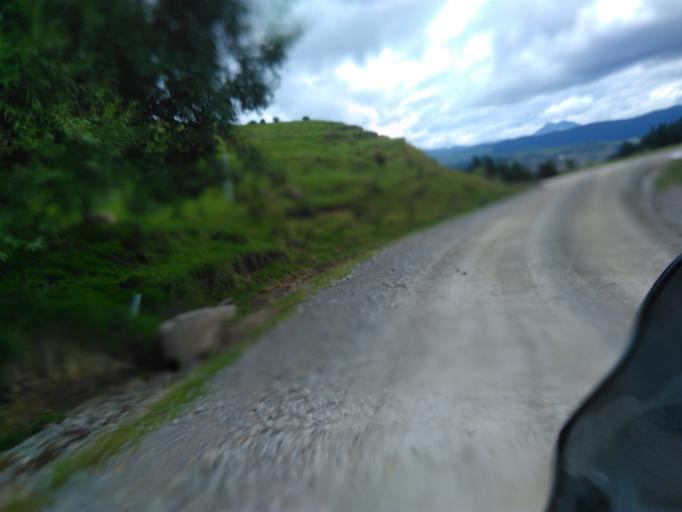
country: NZ
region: Gisborne
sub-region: Gisborne District
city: Gisborne
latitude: -38.0949
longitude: 178.0922
